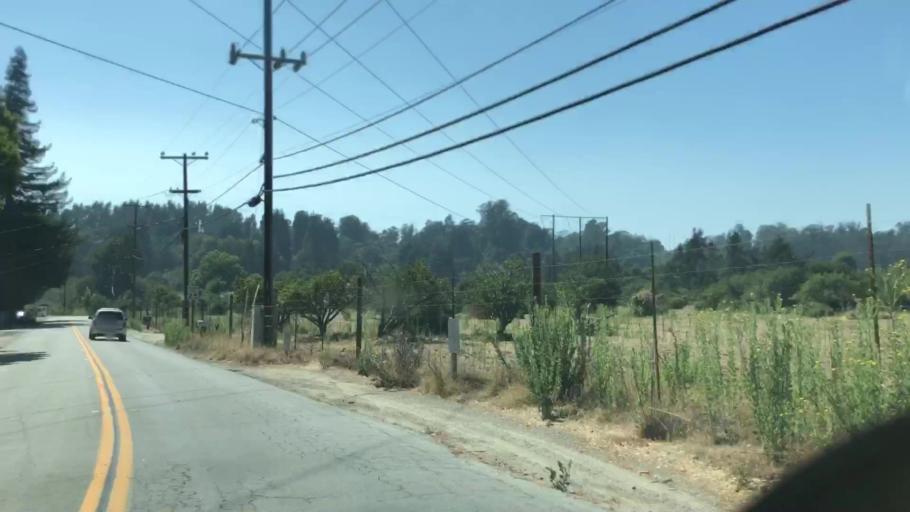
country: US
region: California
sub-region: Santa Cruz County
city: Corralitos
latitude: 36.9905
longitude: -121.8281
